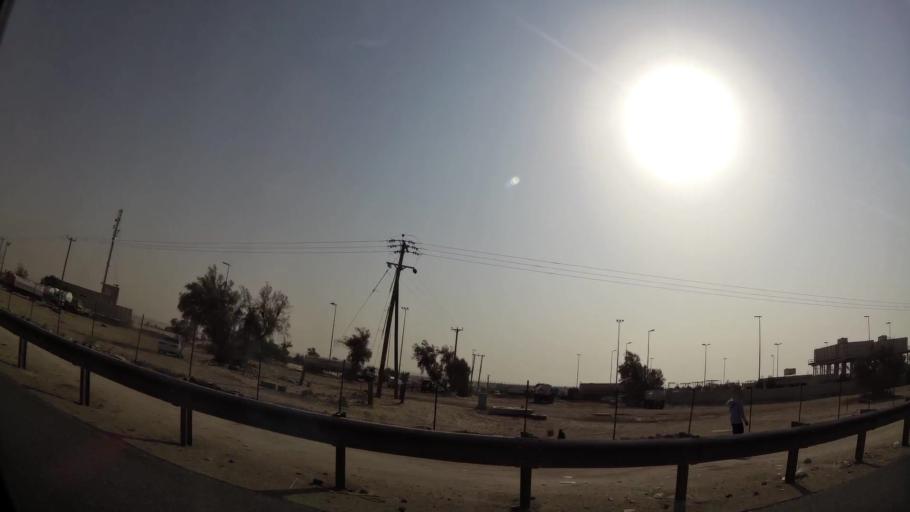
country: KW
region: Muhafazat al Jahra'
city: Al Jahra'
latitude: 29.3121
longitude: 47.7758
